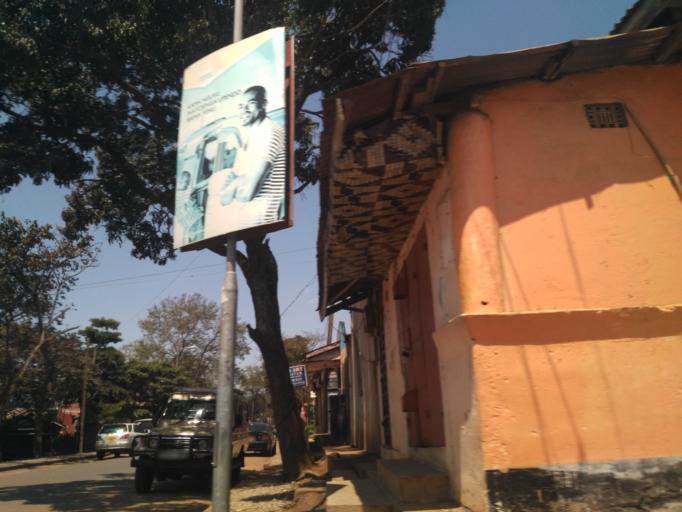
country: TZ
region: Arusha
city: Arusha
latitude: -3.3681
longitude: 36.6868
